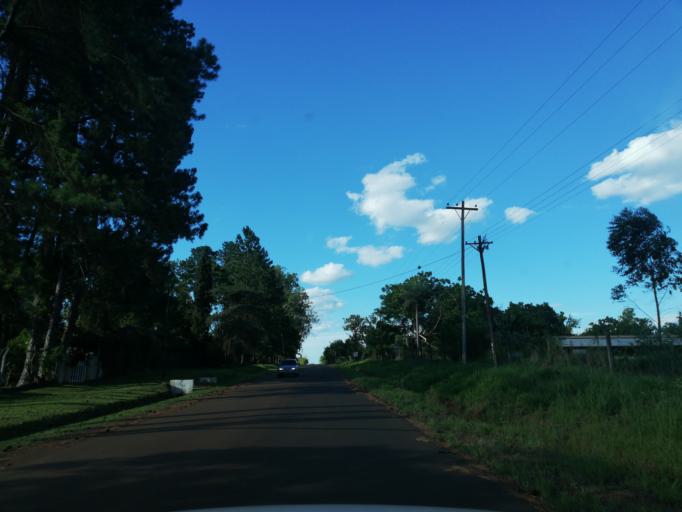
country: AR
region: Misiones
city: Garupa
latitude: -27.4643
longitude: -55.7974
